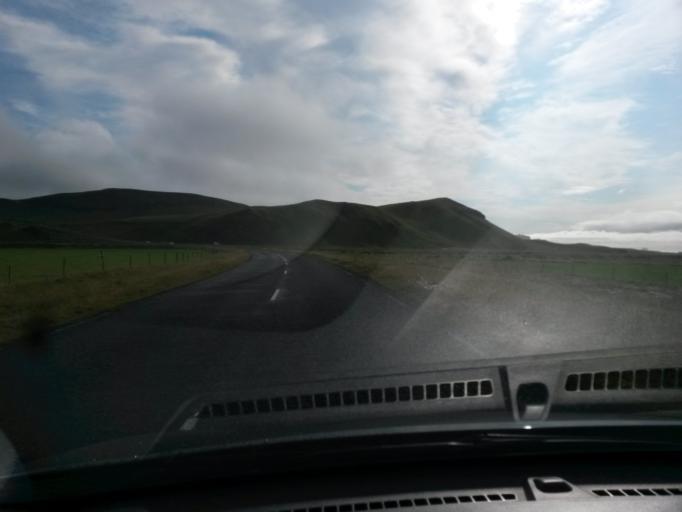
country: IS
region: South
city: Vestmannaeyjar
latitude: 63.4322
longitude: -19.1864
